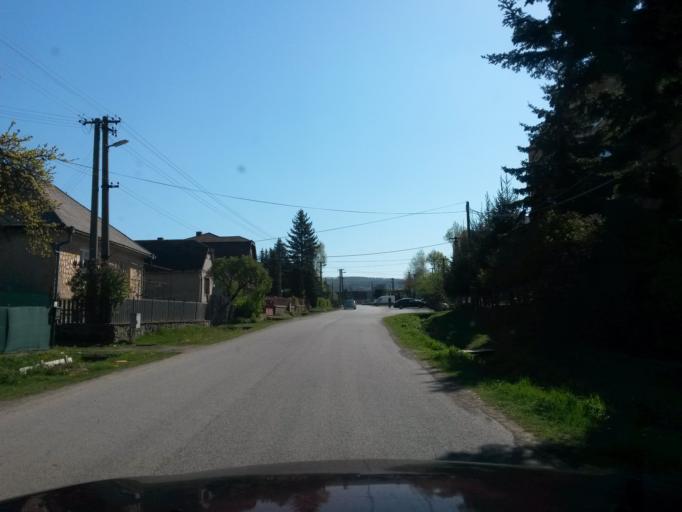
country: SK
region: Kosicky
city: Kosice
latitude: 48.6841
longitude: 21.4332
